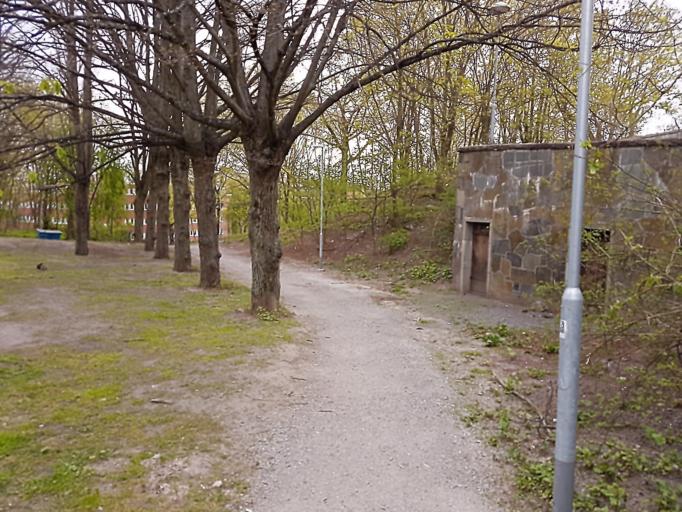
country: SE
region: Stockholm
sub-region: Solna Kommun
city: Solna
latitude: 59.3604
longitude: 18.0147
